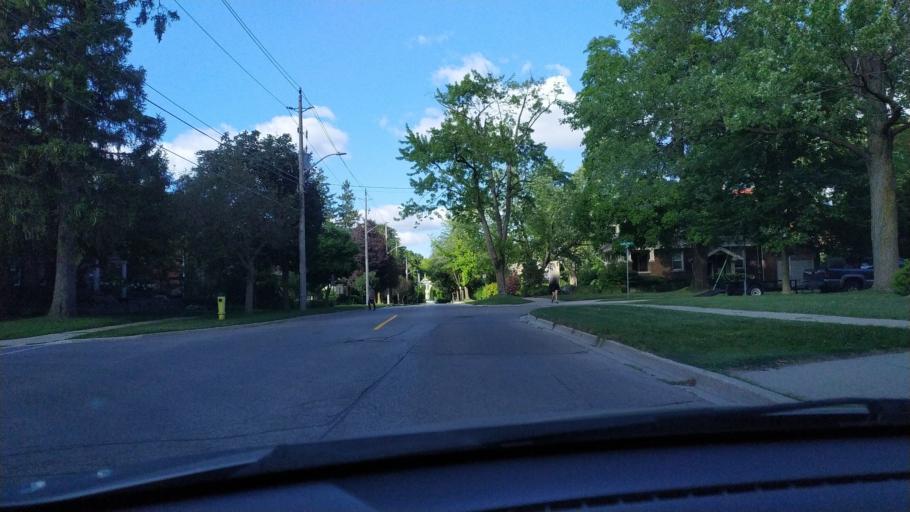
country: CA
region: Ontario
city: Stratford
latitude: 43.3742
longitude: -80.9845
